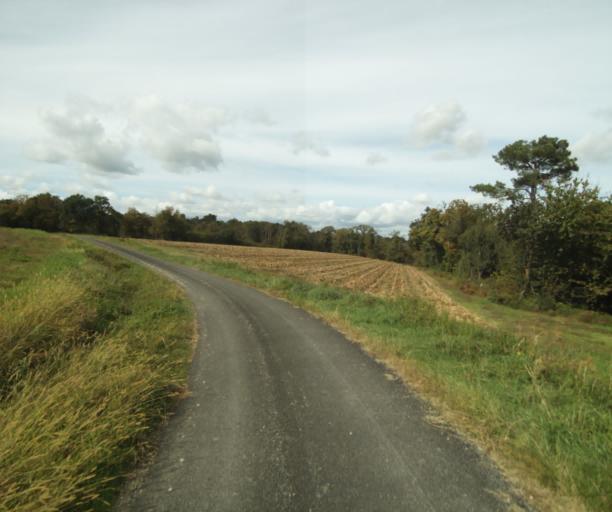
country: FR
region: Midi-Pyrenees
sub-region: Departement du Gers
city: Eauze
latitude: 43.8311
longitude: 0.1037
